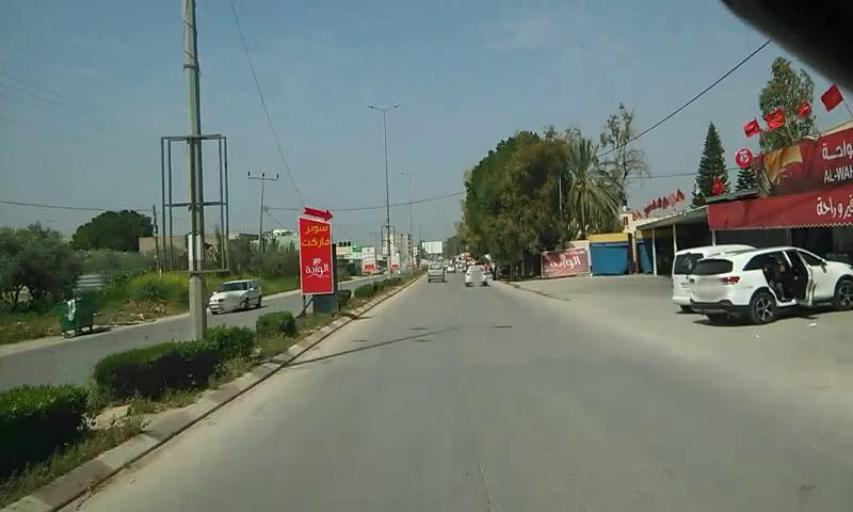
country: PS
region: West Bank
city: Janin
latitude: 32.4747
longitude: 35.3016
